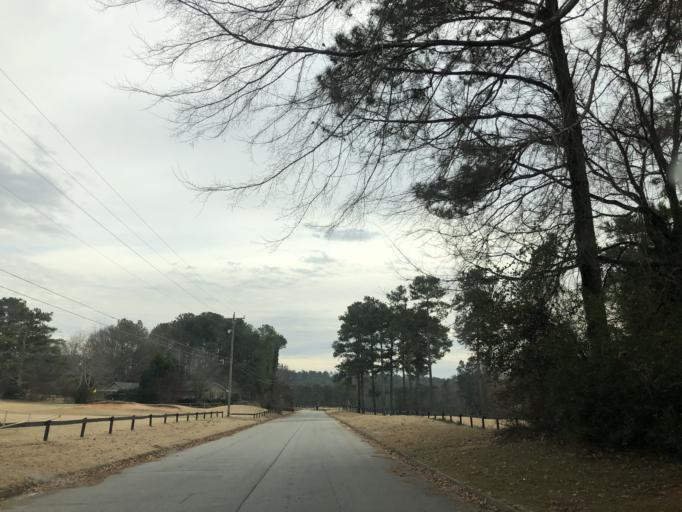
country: US
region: Georgia
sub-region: DeKalb County
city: Pine Mountain
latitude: 33.6390
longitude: -84.1821
